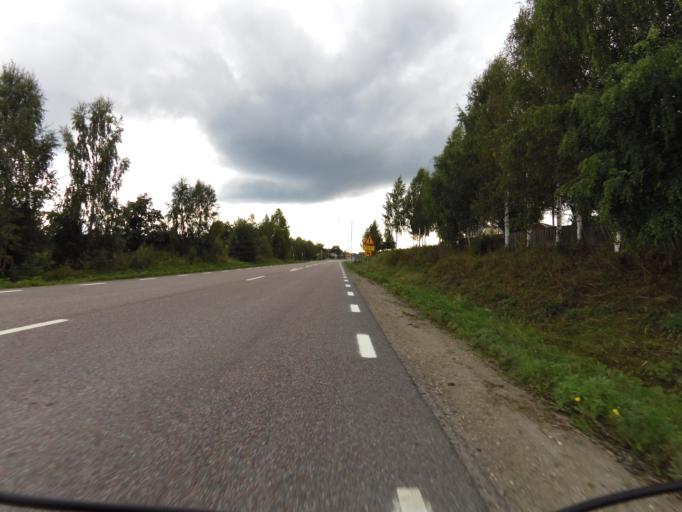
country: SE
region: Gaevleborg
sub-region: Ockelbo Kommun
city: Ockelbo
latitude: 60.8800
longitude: 16.7136
